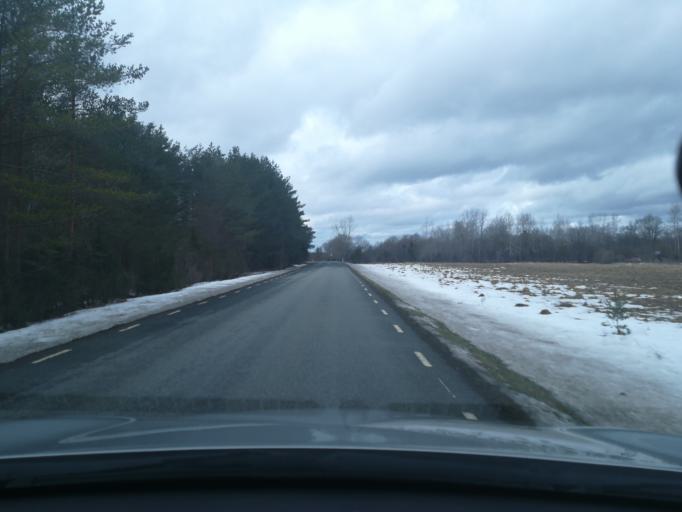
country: EE
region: Harju
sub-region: Saue linn
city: Saue
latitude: 59.3609
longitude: 24.5229
